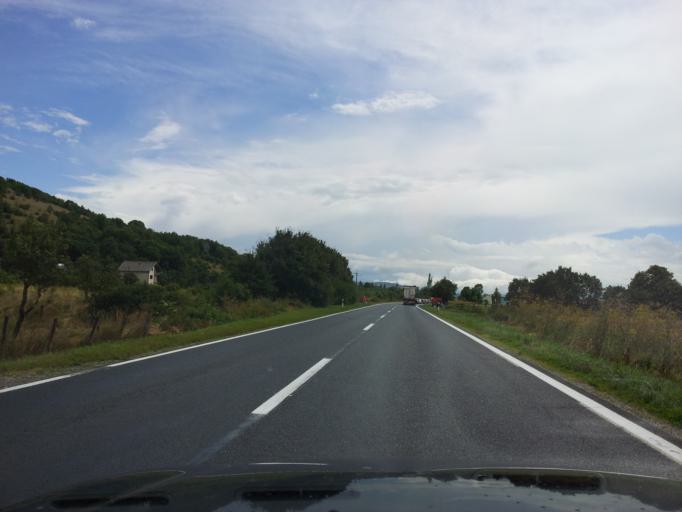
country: BA
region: Federation of Bosnia and Herzegovina
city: Bihac
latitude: 44.5909
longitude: 15.7367
